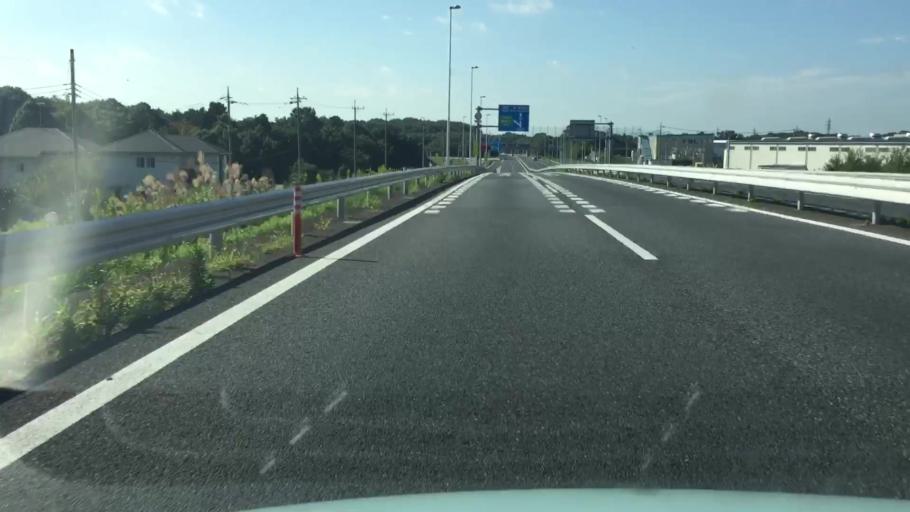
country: JP
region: Tochigi
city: Mooka
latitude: 36.4517
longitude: 139.9770
